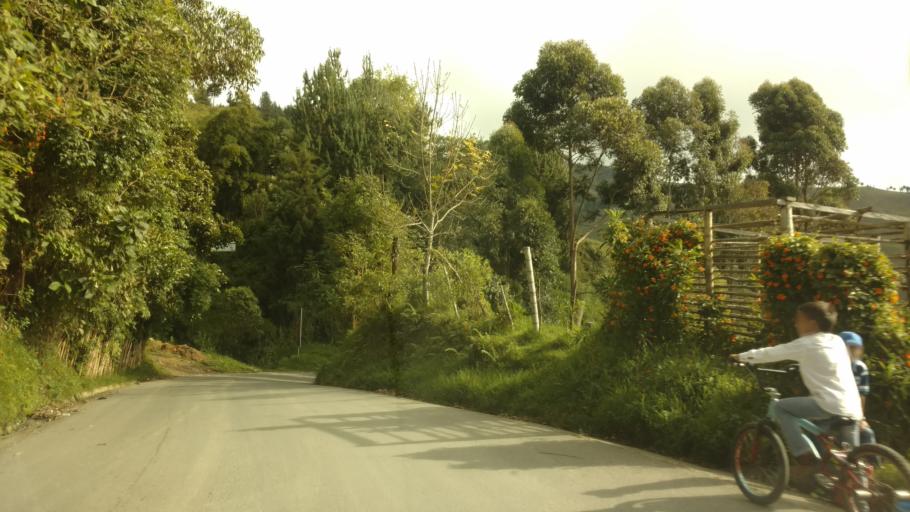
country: CO
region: Caldas
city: Aguadas
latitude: 5.5988
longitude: -75.4498
